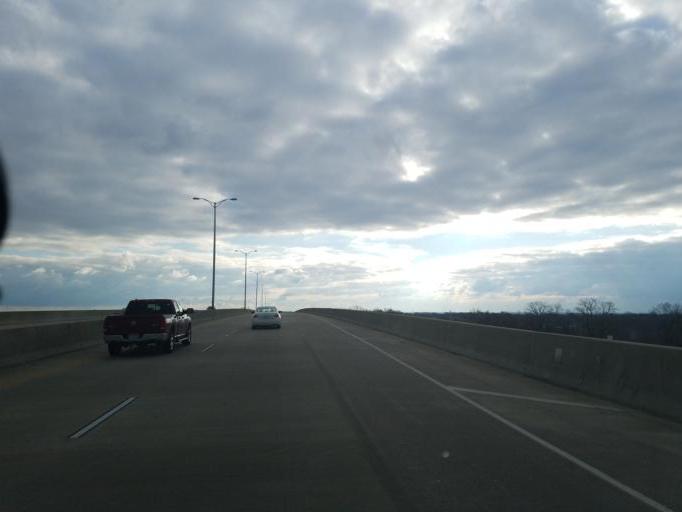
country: US
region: Illinois
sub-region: Madison County
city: Mitchell
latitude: 38.7658
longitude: -90.1370
